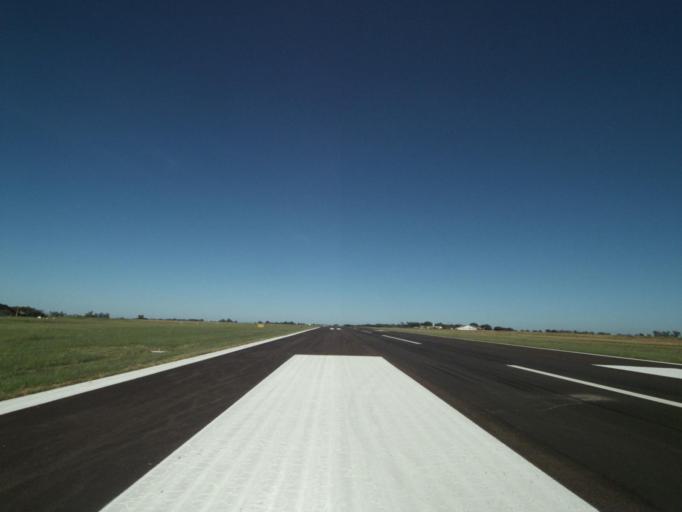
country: BR
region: Rio Grande do Sul
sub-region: Uruguaiana
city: Uruguaiana
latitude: -29.7818
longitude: -57.0334
